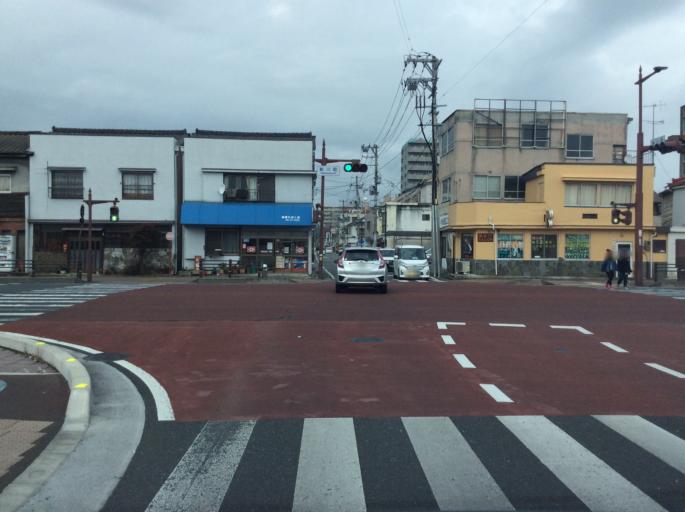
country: JP
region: Fukushima
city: Iwaki
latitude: 37.0536
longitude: 140.8968
